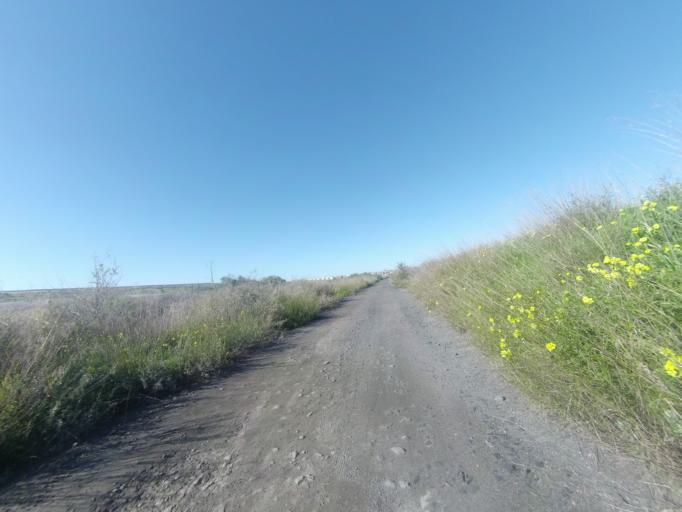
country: ES
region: Andalusia
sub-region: Provincia de Huelva
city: Palos de la Frontera
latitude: 37.2539
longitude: -6.9077
